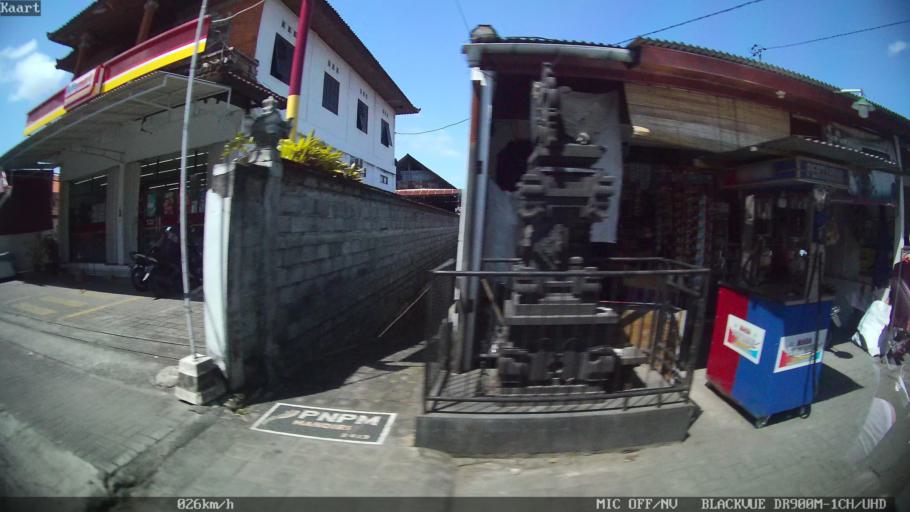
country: ID
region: Bali
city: Banjar Gunungpande
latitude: -8.6548
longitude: 115.1624
